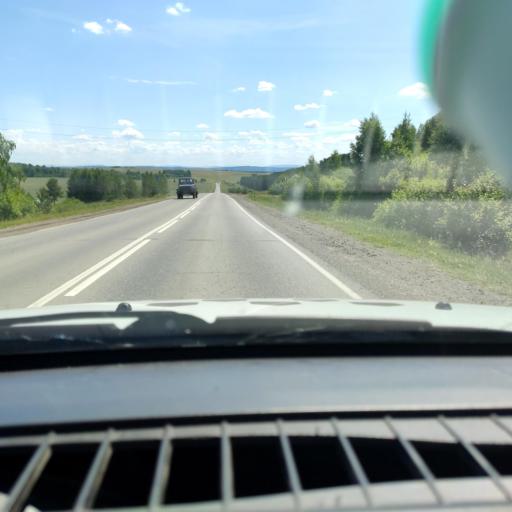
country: RU
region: Bashkortostan
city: Verkhniye Kigi
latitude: 55.3784
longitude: 58.6774
